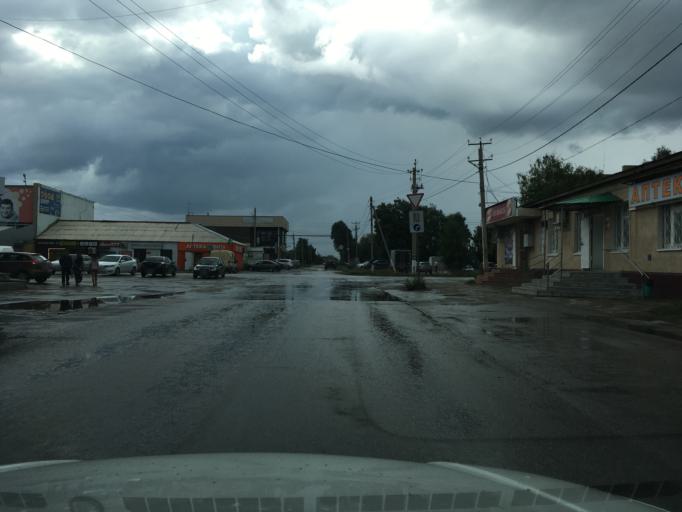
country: RU
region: Samara
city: Bezenchuk
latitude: 52.9805
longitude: 49.4327
